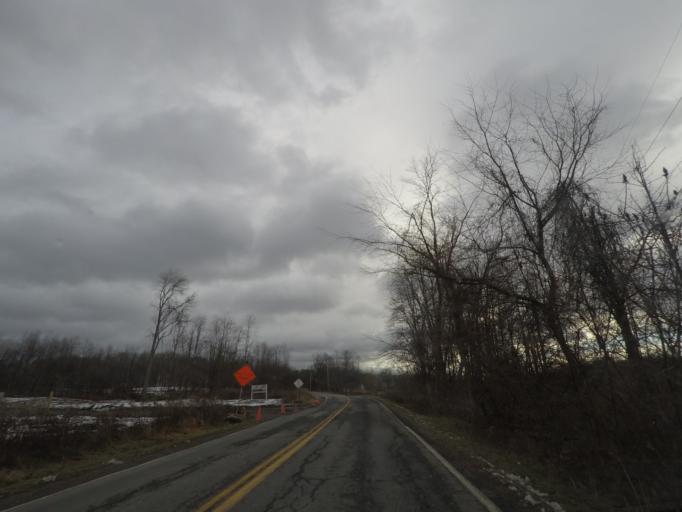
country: US
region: New York
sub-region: Rensselaer County
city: East Greenbush
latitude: 42.5924
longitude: -73.7204
